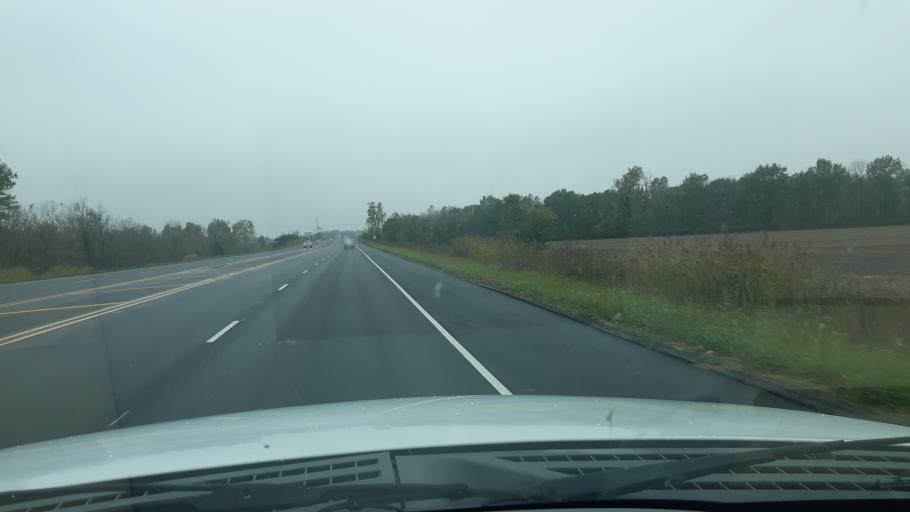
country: US
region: Illinois
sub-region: Saline County
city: Harrisburg
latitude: 37.7489
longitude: -88.5182
